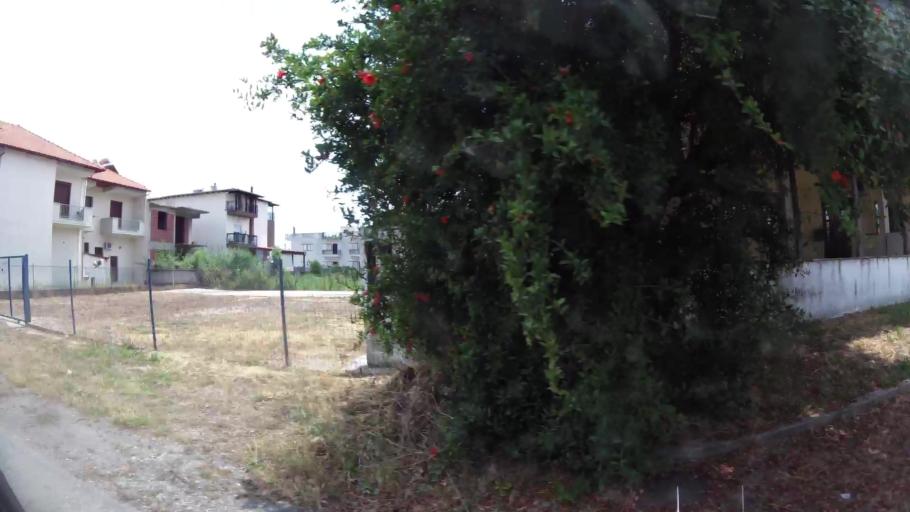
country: GR
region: Central Macedonia
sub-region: Nomos Pierias
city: Kallithea
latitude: 40.2695
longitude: 22.5798
